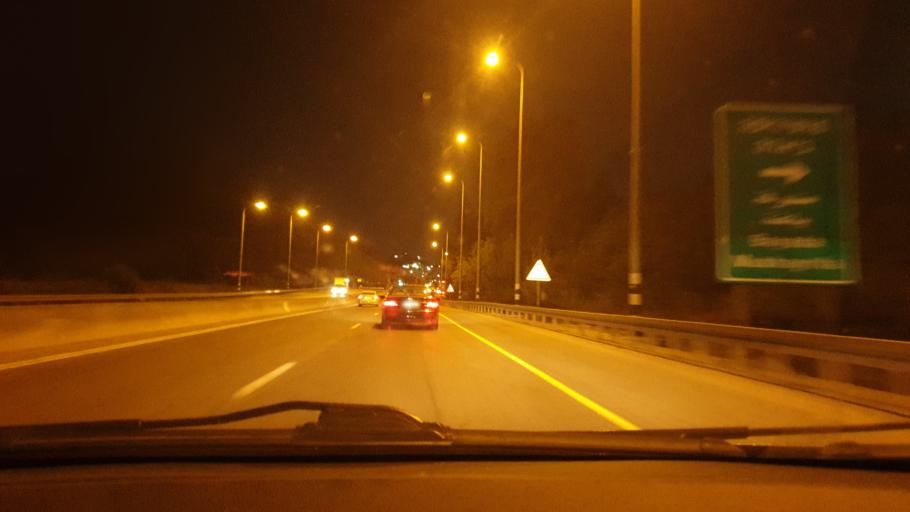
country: IL
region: Haifa
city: Umm el Fahm
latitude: 32.5533
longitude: 35.1658
